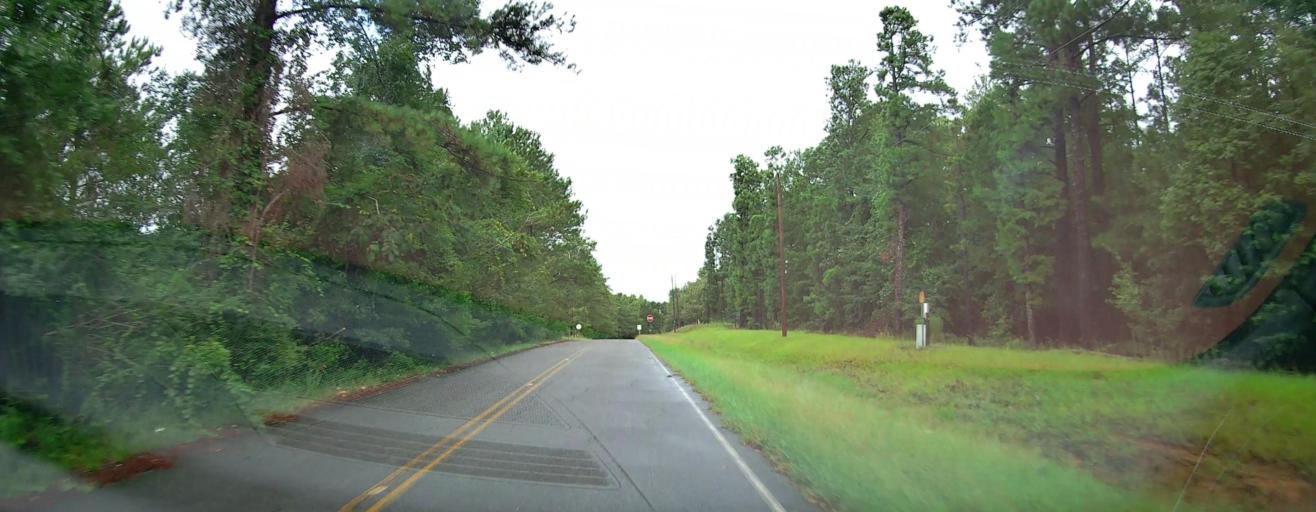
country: US
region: Georgia
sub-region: Bibb County
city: West Point
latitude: 32.7989
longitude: -83.7809
